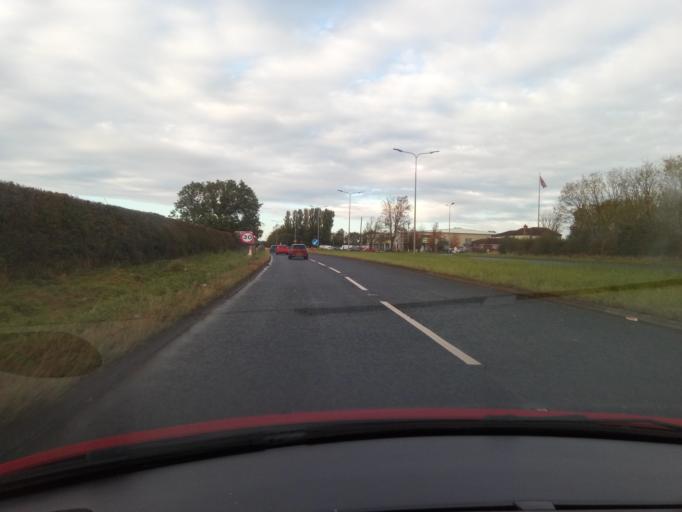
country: GB
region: England
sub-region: Darlington
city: Heighington
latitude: 54.5611
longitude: -1.5968
